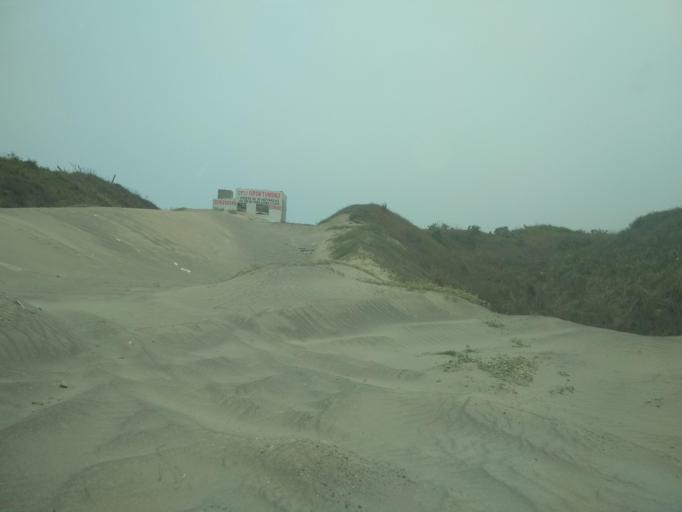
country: MX
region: Veracruz
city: Anton Lizardo
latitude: 19.0542
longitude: -96.0371
